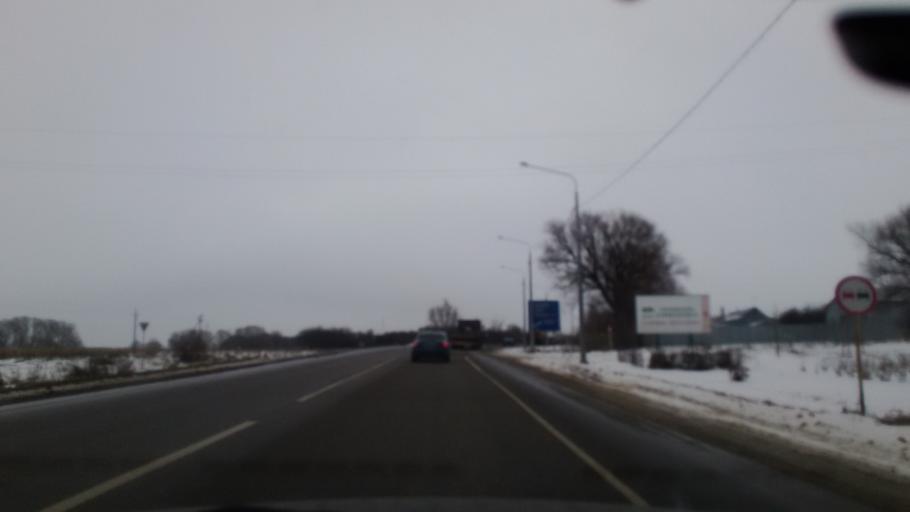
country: RU
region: Tula
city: Borodinskiy
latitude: 54.0281
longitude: 37.8874
